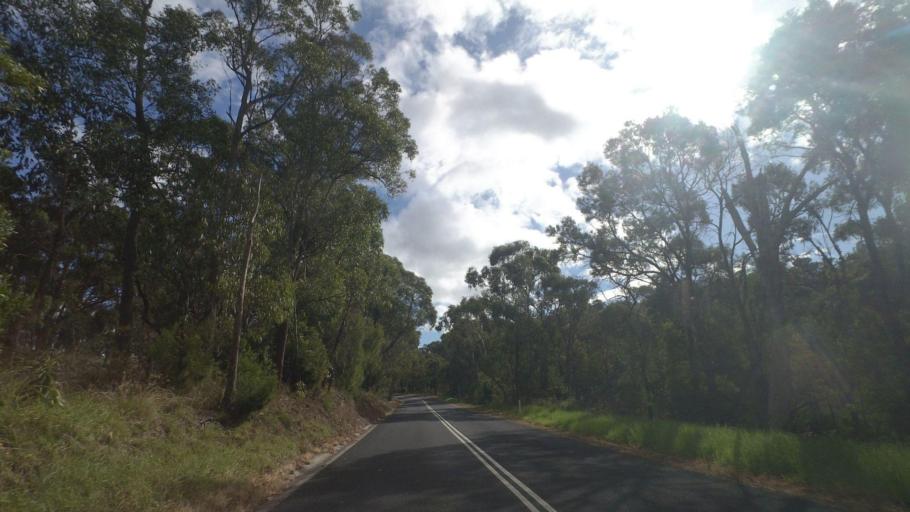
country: AU
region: Victoria
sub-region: Cardinia
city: Garfield
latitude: -38.0534
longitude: 145.6262
